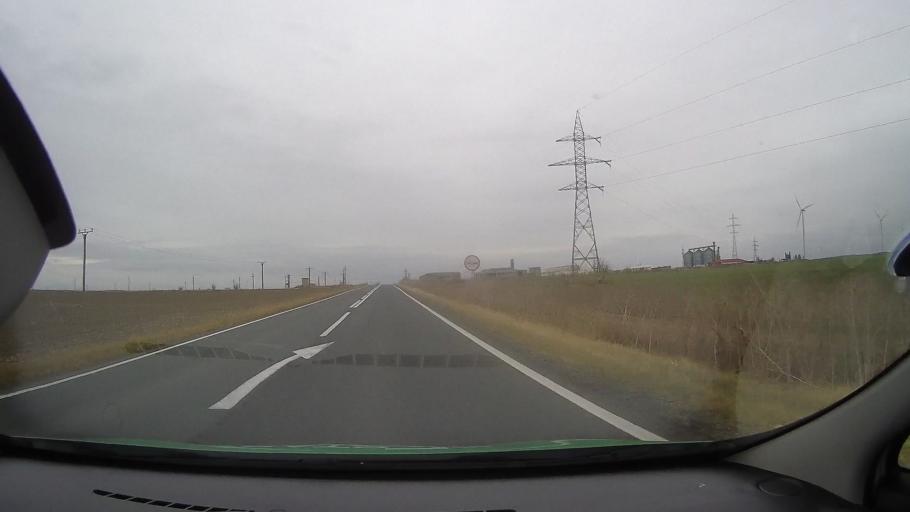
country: RO
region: Constanta
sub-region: Comuna Nicolae Balcescu
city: Dorobantu
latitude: 44.4243
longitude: 28.3098
